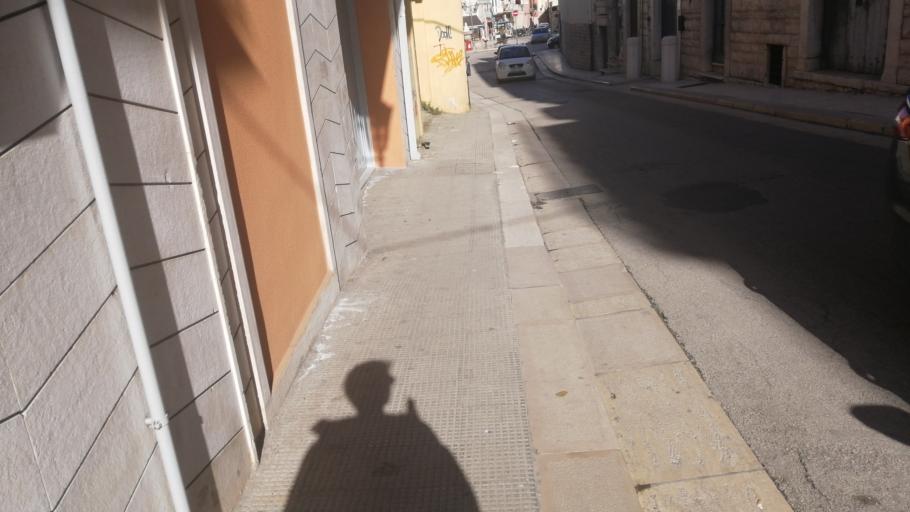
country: IT
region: Apulia
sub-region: Provincia di Barletta - Andria - Trani
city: Andria
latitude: 41.2226
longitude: 16.2932
